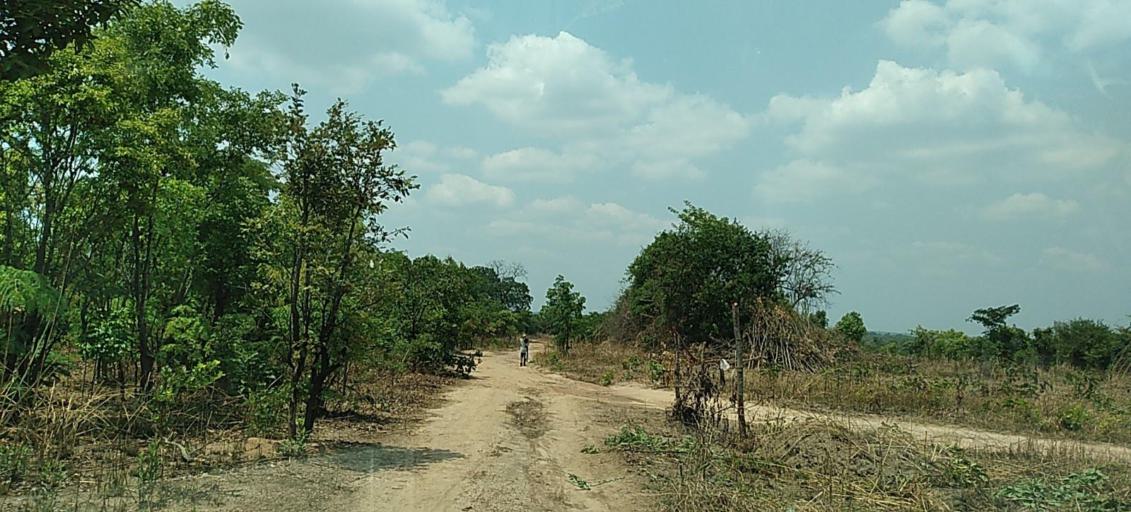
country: ZM
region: Copperbelt
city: Luanshya
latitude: -13.0935
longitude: 28.2876
